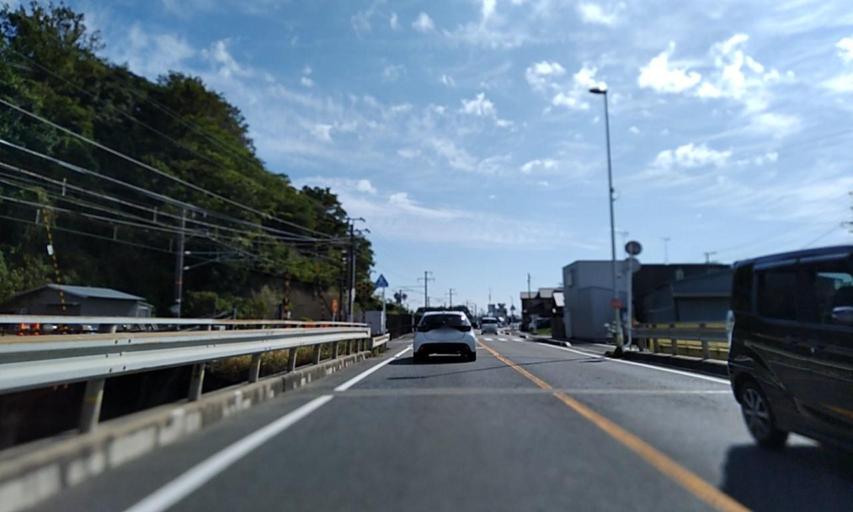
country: JP
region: Wakayama
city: Gobo
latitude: 33.9140
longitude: 135.1487
